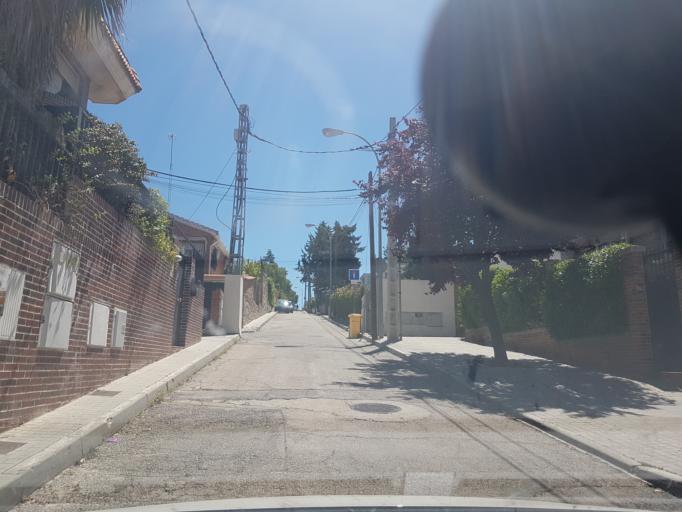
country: ES
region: Madrid
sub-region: Provincia de Madrid
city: Pozuelo de Alarcon
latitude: 40.4417
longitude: -3.8125
